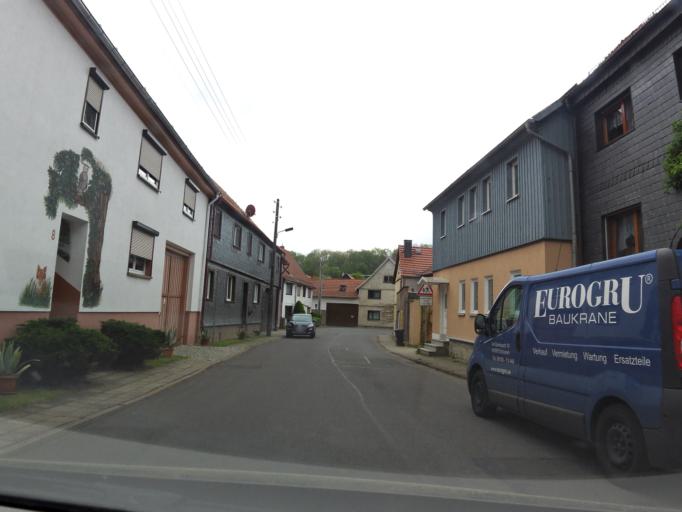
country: DE
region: Thuringia
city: Ernstroda
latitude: 50.8655
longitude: 10.6203
